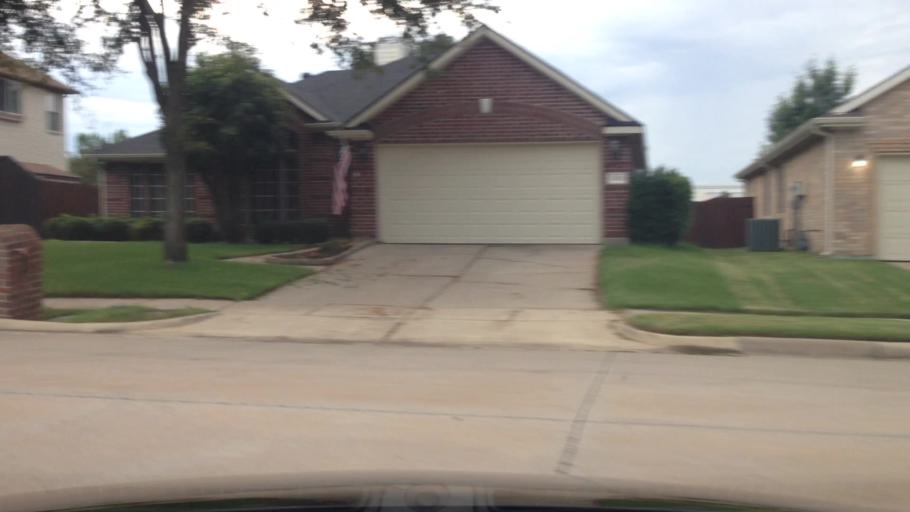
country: US
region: Texas
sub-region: Denton County
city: Flower Mound
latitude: 33.0018
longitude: -97.0575
